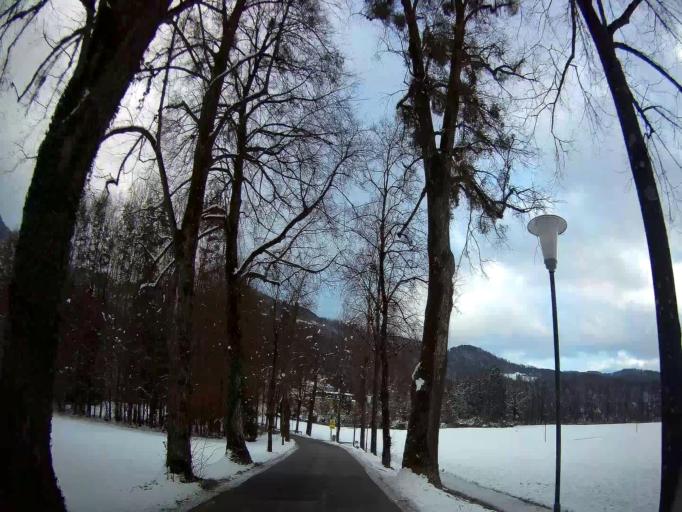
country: AT
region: Salzburg
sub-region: Politischer Bezirk Salzburg-Umgebung
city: Elsbethen
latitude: 47.7869
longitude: 13.0852
